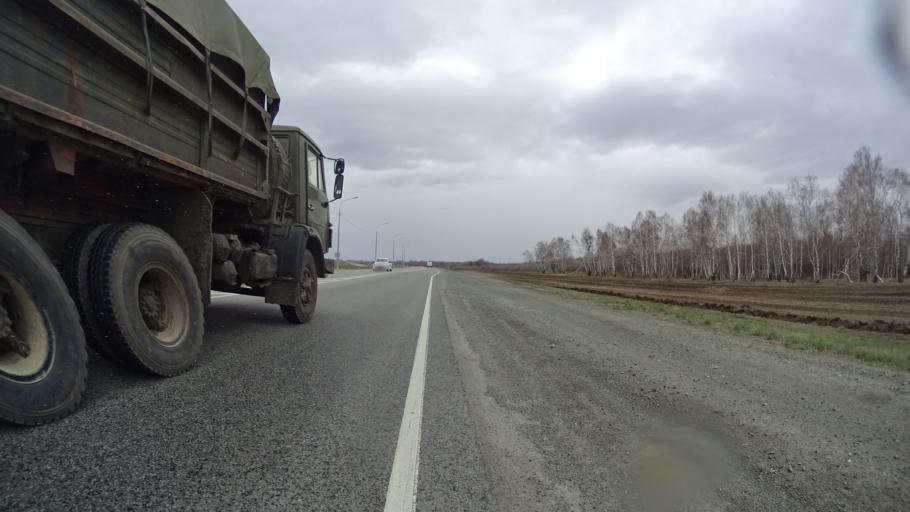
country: RU
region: Chelyabinsk
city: Krasnogorskiy
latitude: 54.6826
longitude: 61.2470
